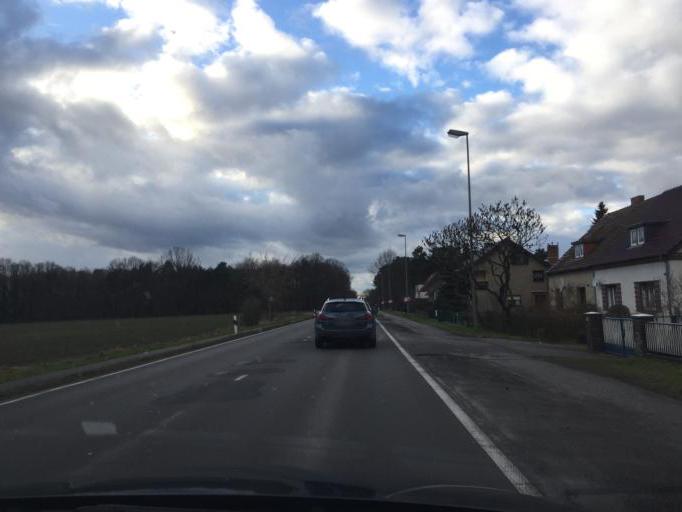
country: DE
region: Brandenburg
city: Kolkwitz
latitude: 51.7507
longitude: 14.2728
